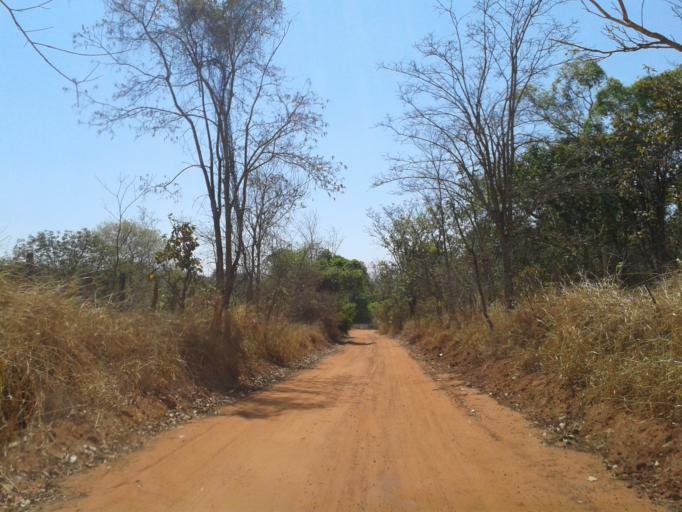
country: BR
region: Minas Gerais
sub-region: Ituiutaba
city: Ituiutaba
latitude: -19.0881
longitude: -49.2989
